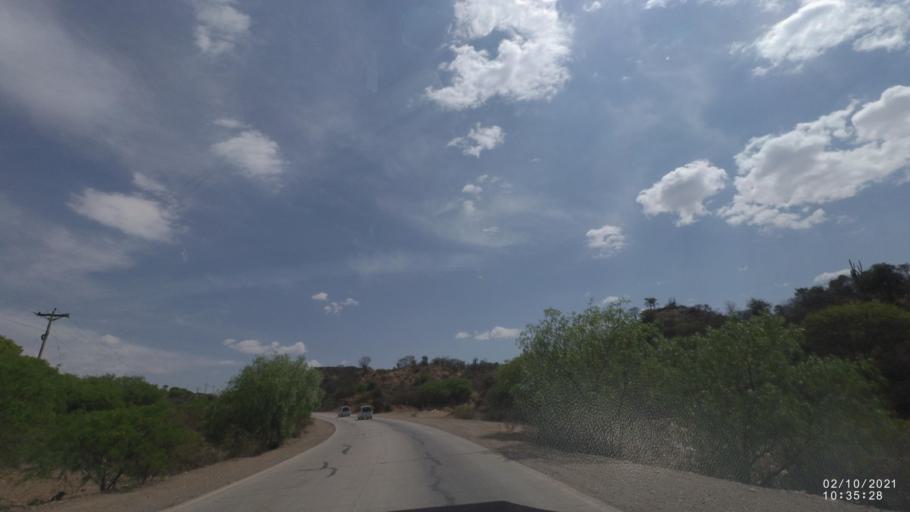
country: BO
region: Cochabamba
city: Capinota
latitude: -17.6607
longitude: -66.2575
